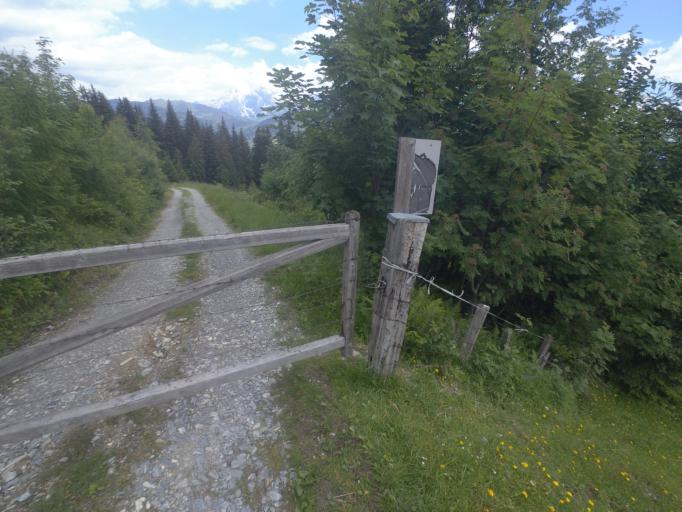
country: AT
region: Salzburg
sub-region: Politischer Bezirk Sankt Johann im Pongau
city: Schwarzach im Pongau
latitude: 47.3026
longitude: 13.1630
